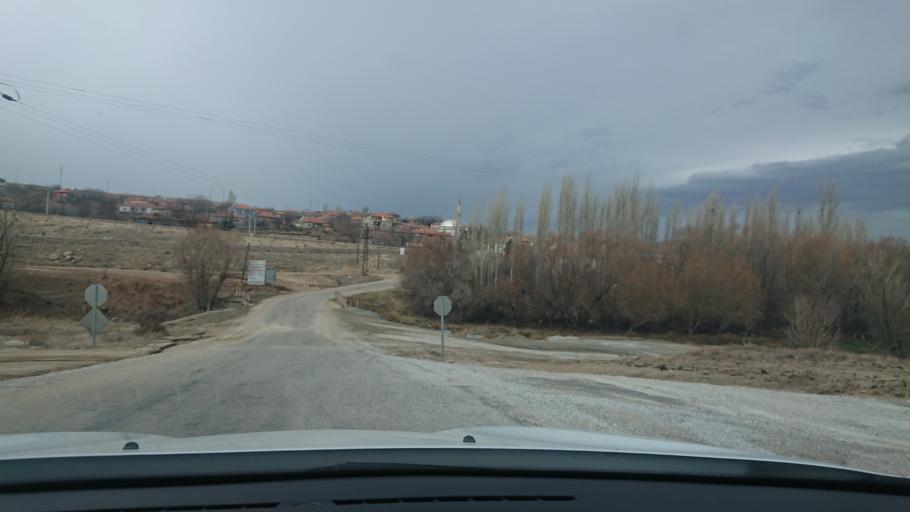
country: TR
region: Aksaray
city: Agacoren
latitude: 38.9188
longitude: 33.9283
